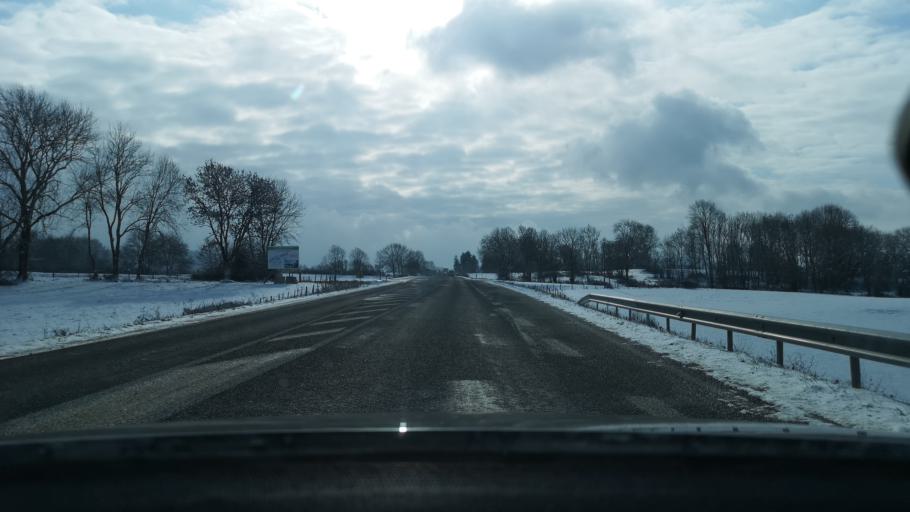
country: FR
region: Franche-Comte
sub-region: Departement du Jura
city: Orgelet
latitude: 46.5601
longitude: 5.5955
